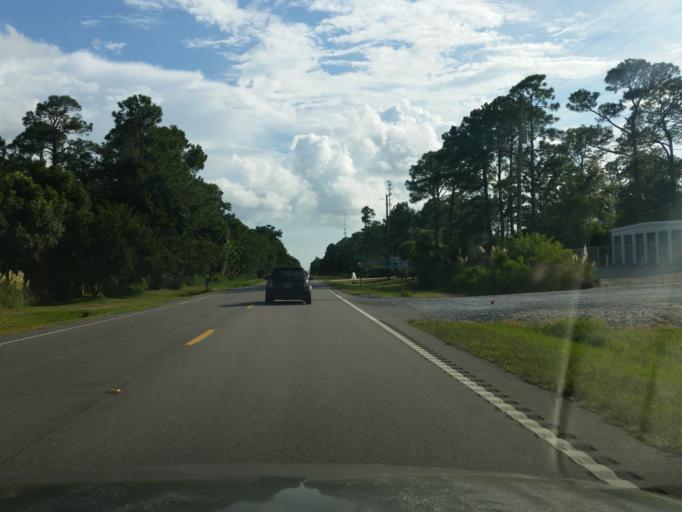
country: US
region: Alabama
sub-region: Mobile County
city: Dauphin Island
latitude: 30.3688
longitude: -88.1115
